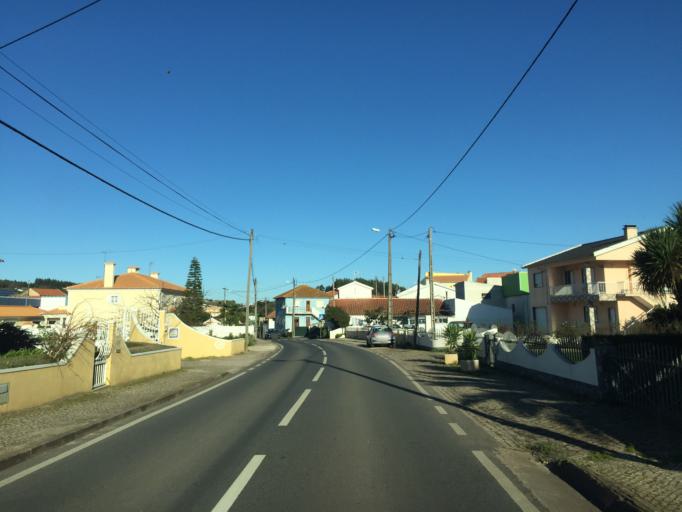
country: PT
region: Lisbon
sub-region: Sintra
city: Almargem
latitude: 38.8403
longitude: -9.2560
